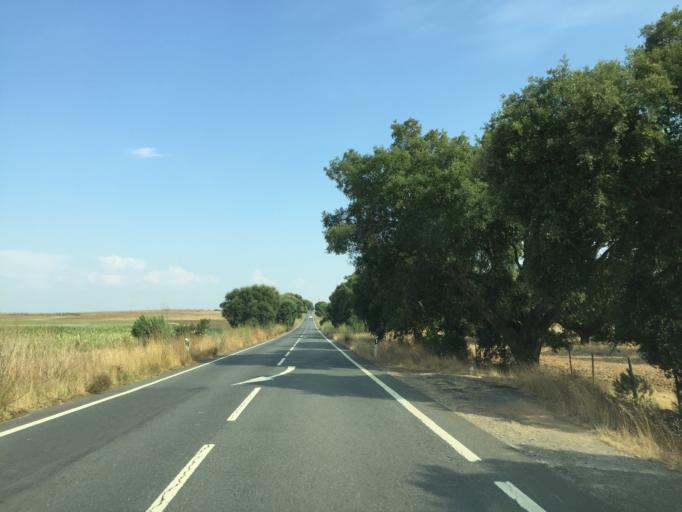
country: PT
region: Beja
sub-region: Aljustrel
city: Aljustrel
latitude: 37.9331
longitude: -8.3512
